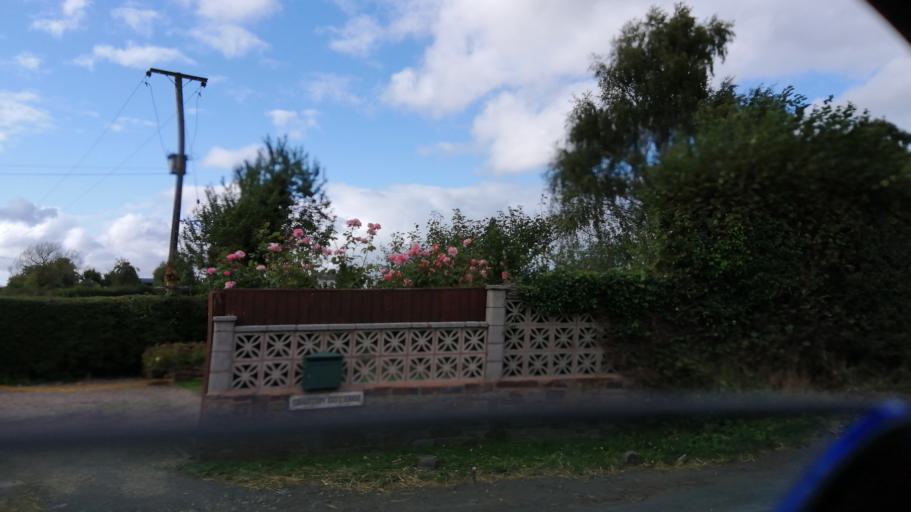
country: GB
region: England
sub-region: Herefordshire
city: Callow
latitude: 52.0190
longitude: -2.7290
